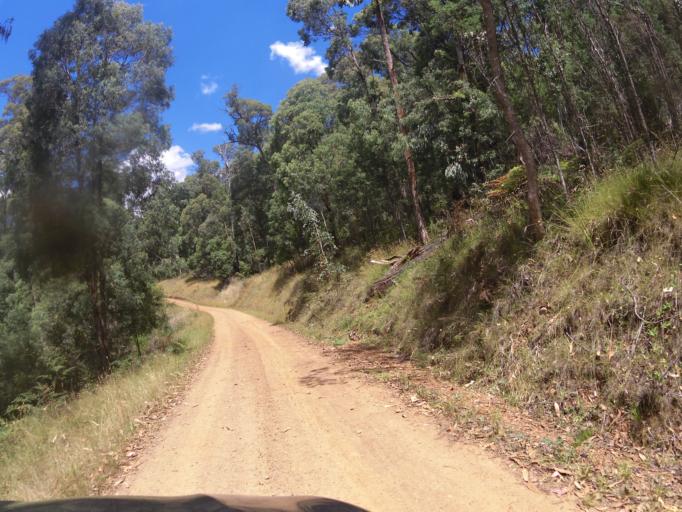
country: AU
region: Victoria
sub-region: Alpine
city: Mount Beauty
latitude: -36.7879
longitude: 147.0782
